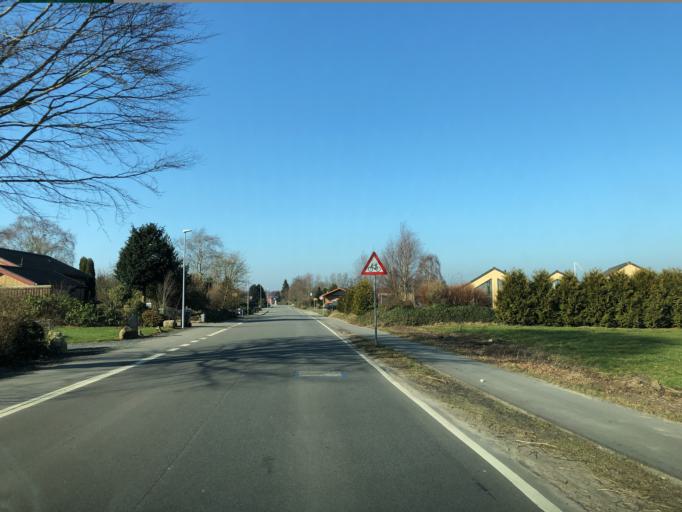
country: DK
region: Central Jutland
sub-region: Silkeborg Kommune
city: Silkeborg
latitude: 56.1533
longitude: 9.4501
